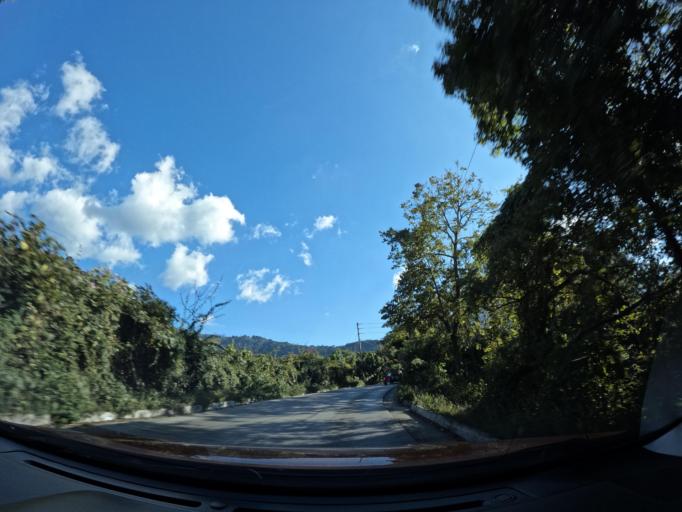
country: GT
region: Sacatepequez
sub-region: Municipio de Santa Maria de Jesus
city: Santa Maria de Jesus
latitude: 14.5251
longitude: -90.7254
